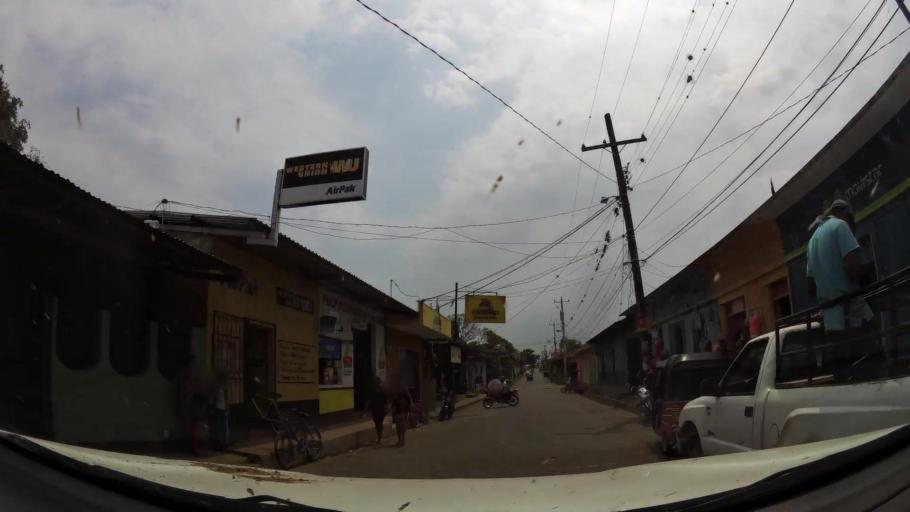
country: NI
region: Granada
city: Diriomo
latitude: 11.8753
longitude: -86.0496
